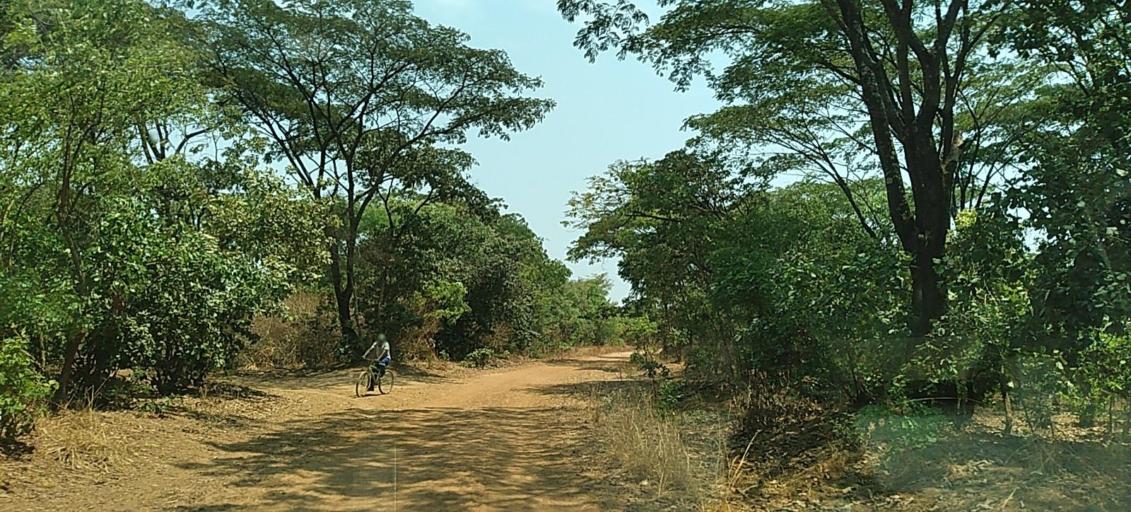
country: ZM
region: Copperbelt
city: Ndola
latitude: -13.0488
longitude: 28.7372
